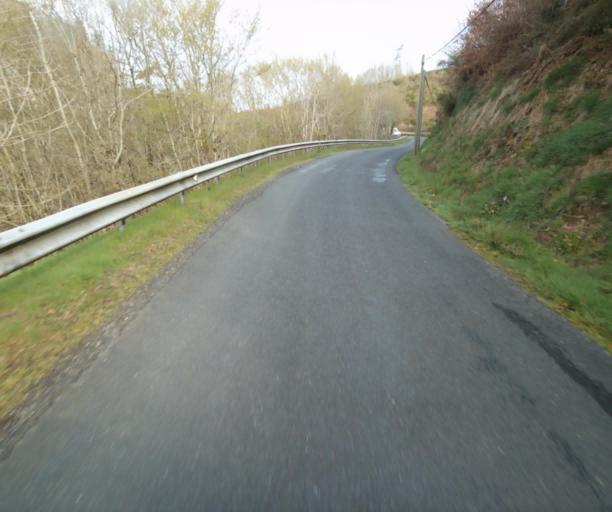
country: FR
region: Limousin
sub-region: Departement de la Correze
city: Naves
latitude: 45.3450
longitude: 1.8186
